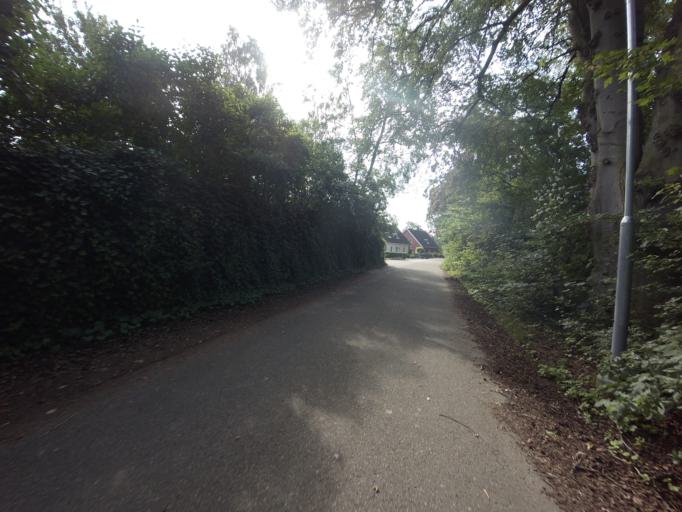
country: SE
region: Skane
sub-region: Malmo
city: Tygelsjo
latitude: 55.4967
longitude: 13.0084
